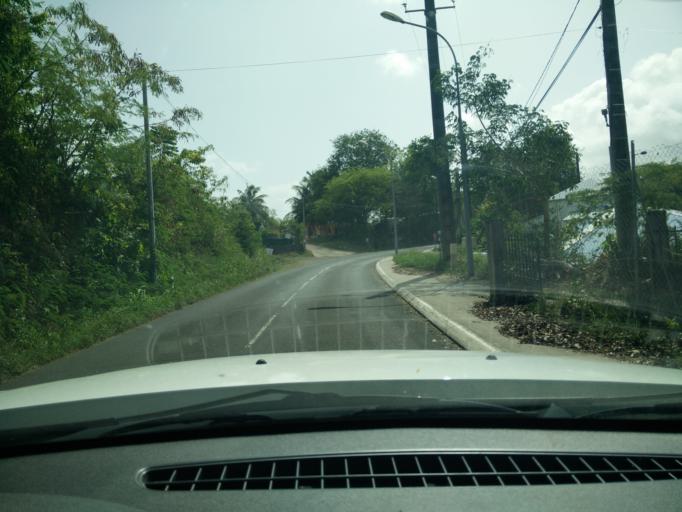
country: GP
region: Guadeloupe
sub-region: Guadeloupe
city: Le Gosier
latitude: 16.2164
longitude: -61.4512
